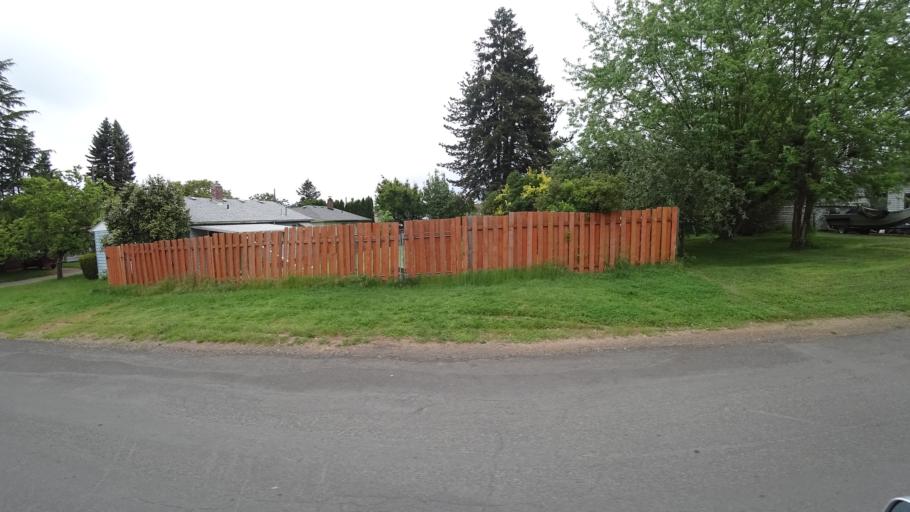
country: US
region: Oregon
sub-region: Multnomah County
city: Portland
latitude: 45.5529
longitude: -122.6123
